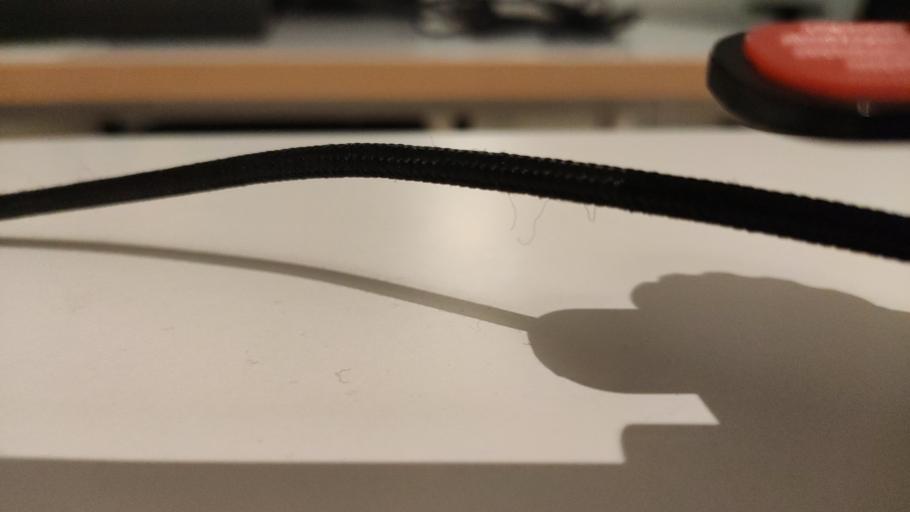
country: RU
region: Moskovskaya
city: Rogachevo
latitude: 56.4047
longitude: 37.2450
